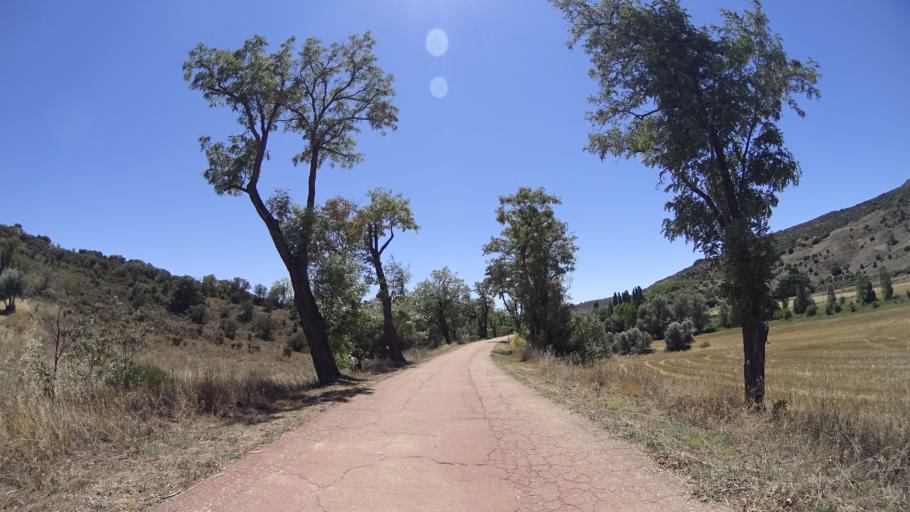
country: ES
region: Madrid
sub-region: Provincia de Madrid
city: Ambite
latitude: 40.2999
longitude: -3.1930
